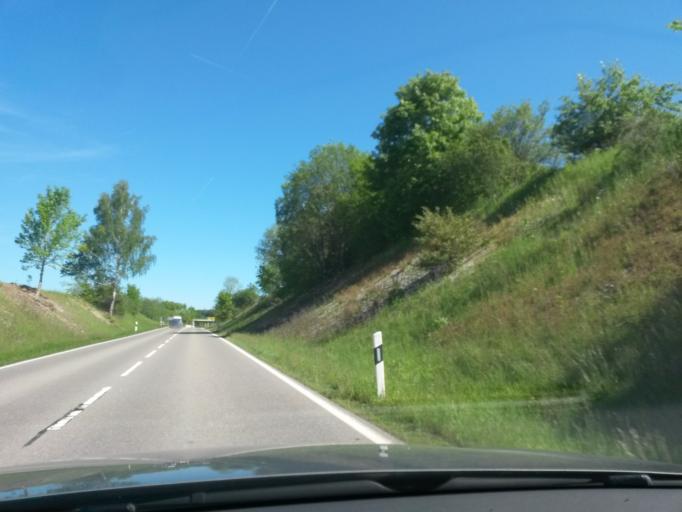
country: DE
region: Baden-Wuerttemberg
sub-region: Tuebingen Region
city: Trochtelfingen
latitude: 48.2713
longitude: 9.2784
